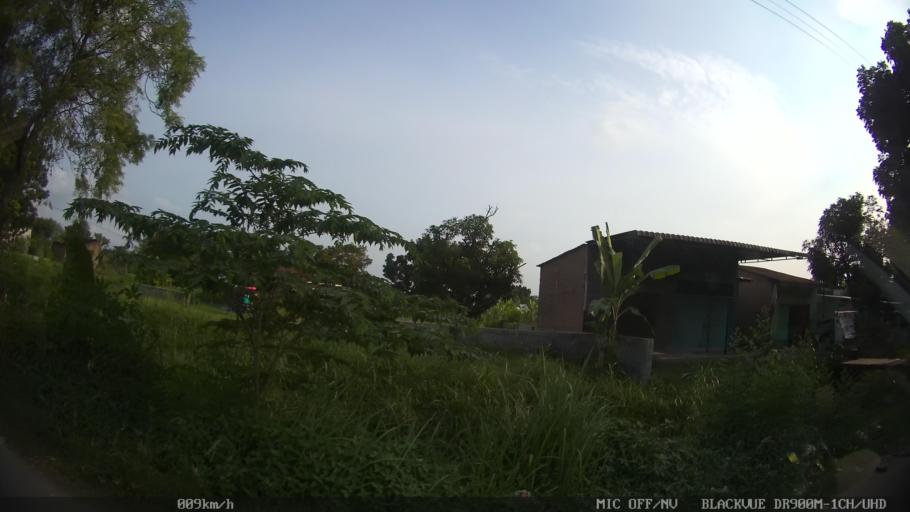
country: ID
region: North Sumatra
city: Medan
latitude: 3.5813
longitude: 98.7532
